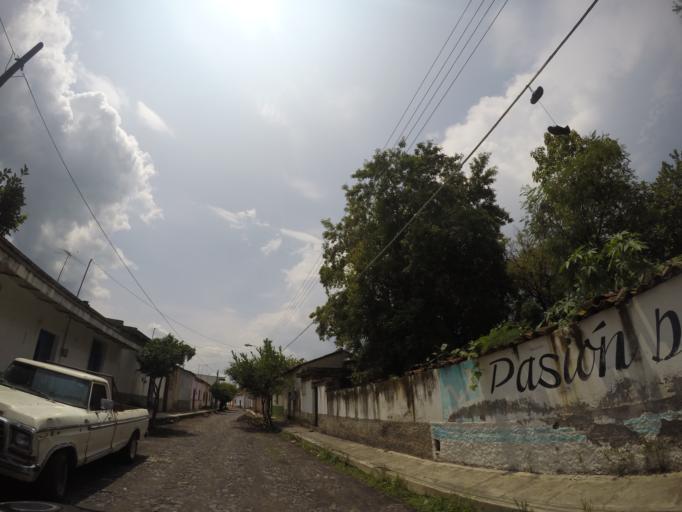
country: MX
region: Nayarit
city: Jala
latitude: 21.1060
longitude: -104.4371
